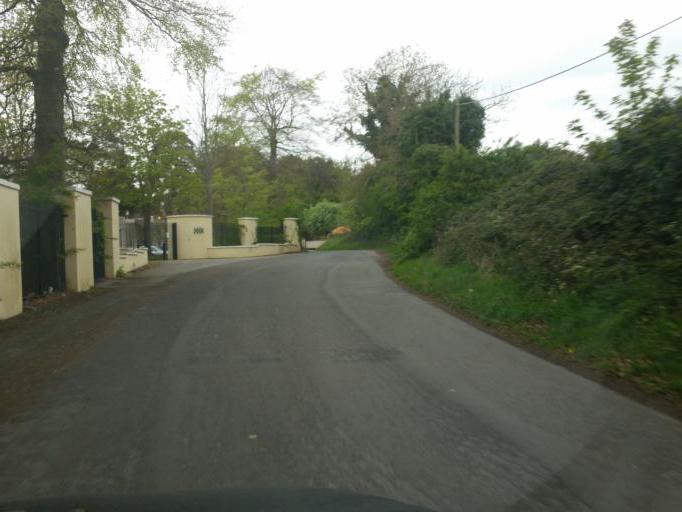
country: IE
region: Leinster
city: Castleknock
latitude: 53.3803
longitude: -6.3354
